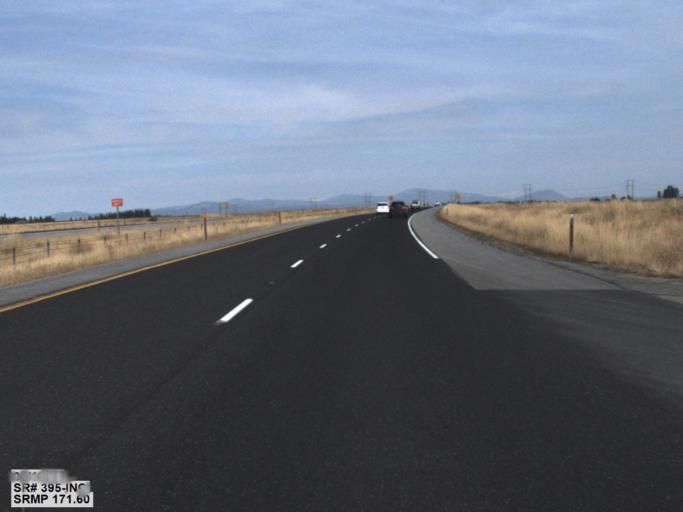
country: US
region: Washington
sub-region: Spokane County
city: Fairwood
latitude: 47.8384
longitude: -117.4218
